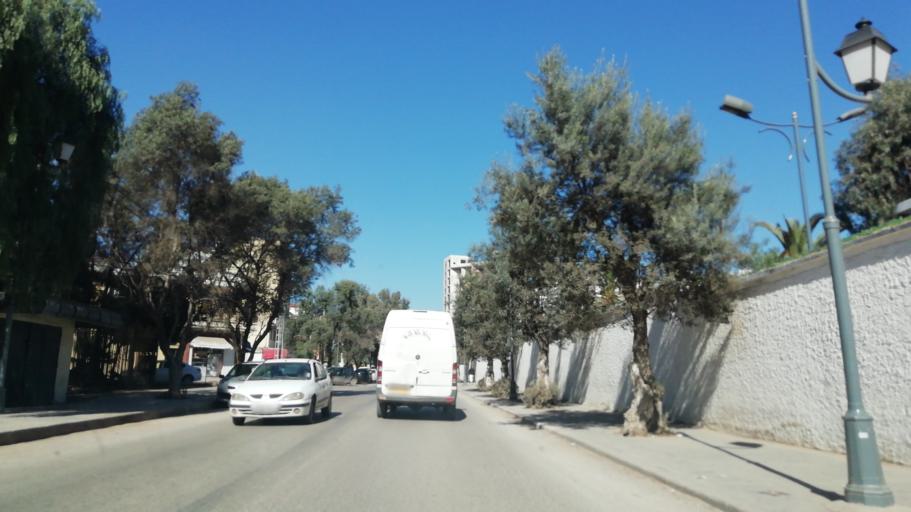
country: DZ
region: Oran
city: Oran
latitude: 35.6940
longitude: -0.6107
